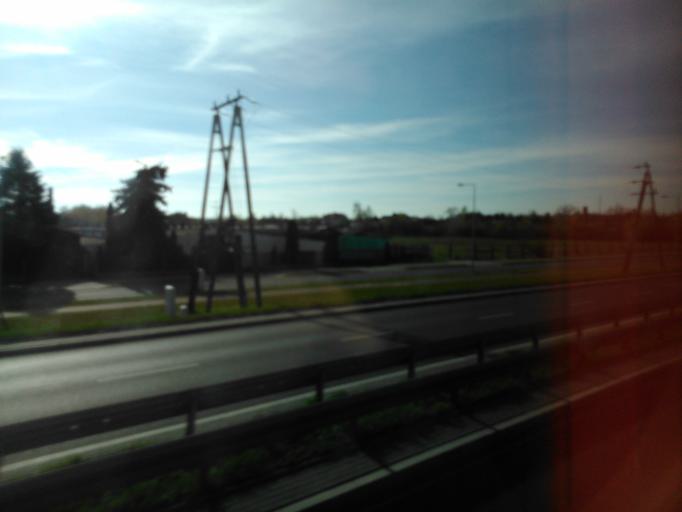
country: PL
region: Kujawsko-Pomorskie
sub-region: Torun
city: Torun
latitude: 53.0033
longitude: 18.6575
